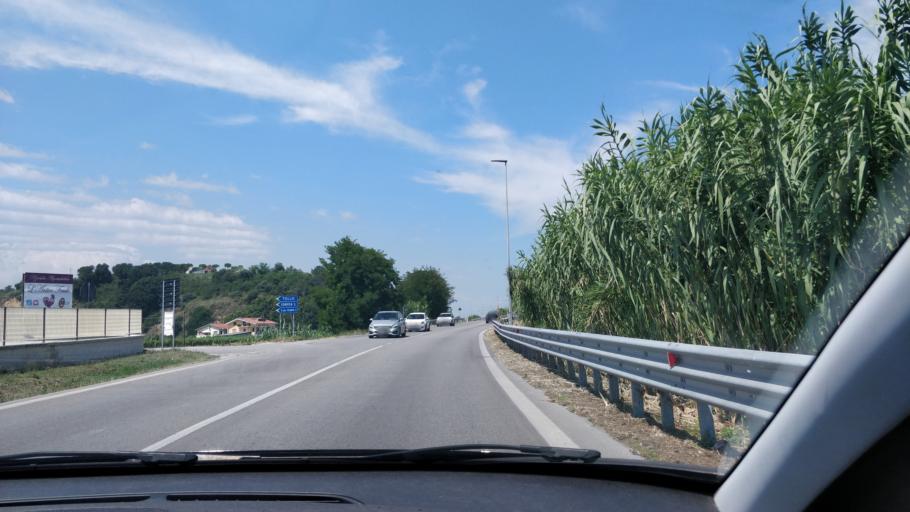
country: IT
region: Abruzzo
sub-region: Provincia di Chieti
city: Tollo
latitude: 42.3844
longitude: 14.3584
